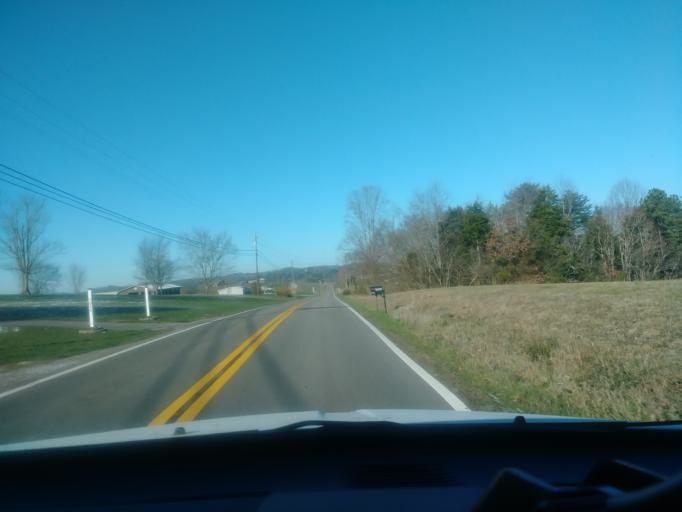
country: US
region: Tennessee
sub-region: Greene County
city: Mosheim
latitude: 36.1174
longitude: -82.9844
